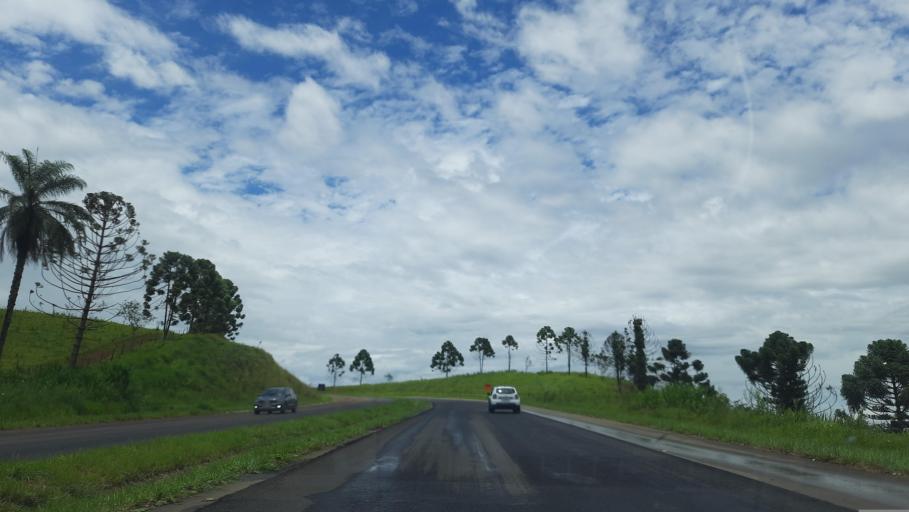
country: BR
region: Minas Gerais
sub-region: Pocos De Caldas
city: Pocos de Caldas
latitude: -21.8352
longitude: -46.6712
